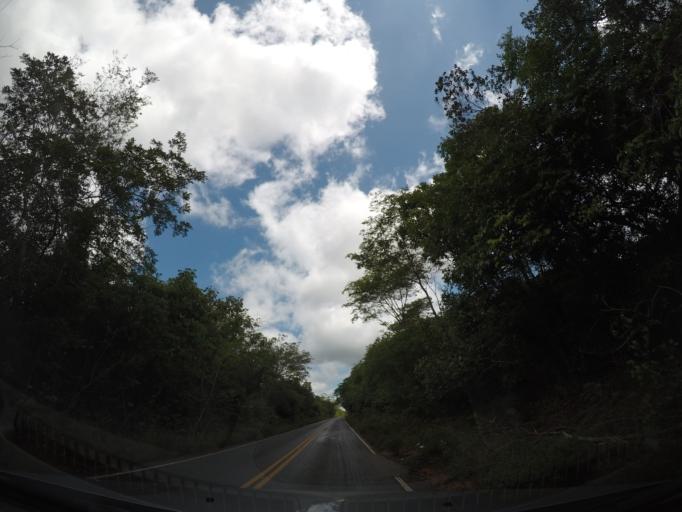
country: BR
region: Bahia
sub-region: Andarai
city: Vera Cruz
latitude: -12.5245
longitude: -41.3633
